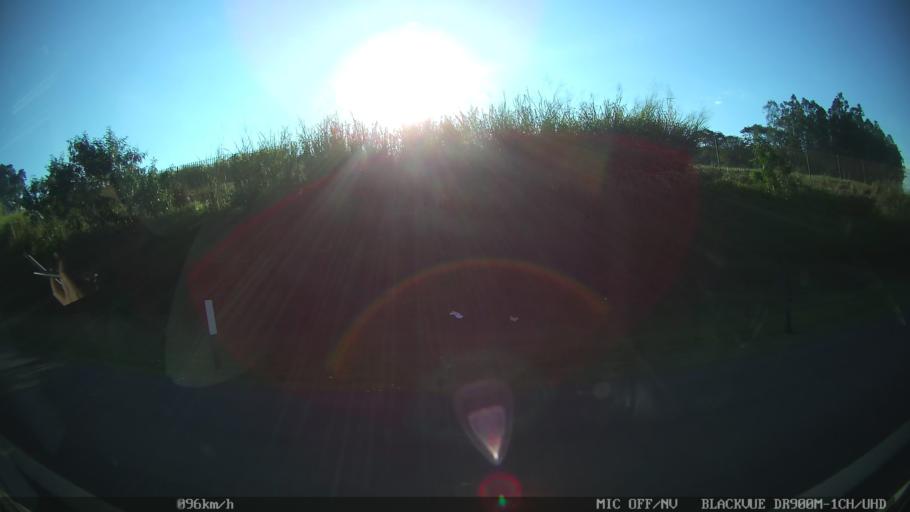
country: BR
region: Sao Paulo
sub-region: Piracicaba
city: Piracicaba
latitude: -22.6979
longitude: -47.6387
